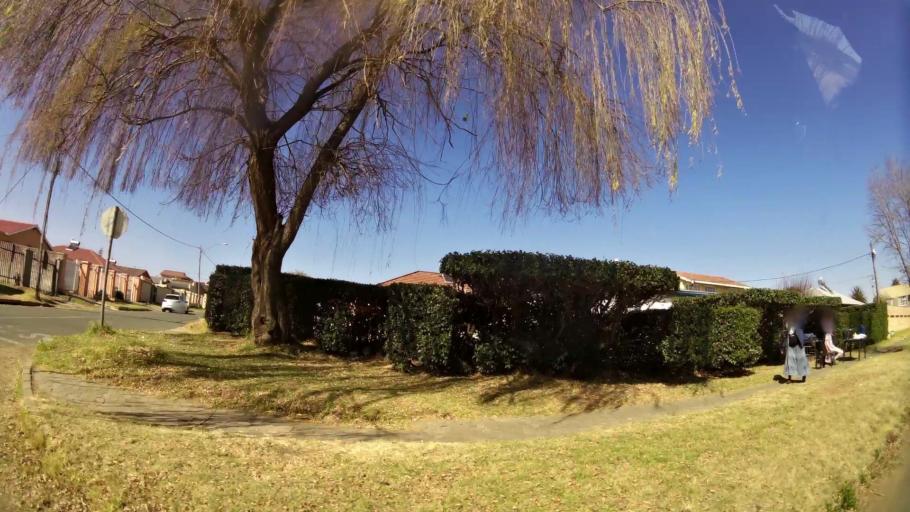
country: ZA
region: Gauteng
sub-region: City of Johannesburg Metropolitan Municipality
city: Johannesburg
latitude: -26.1936
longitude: 27.9559
